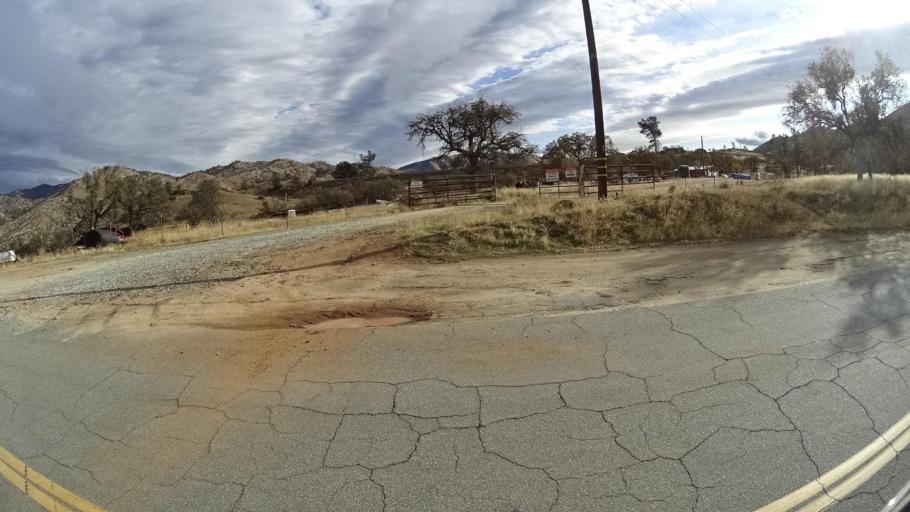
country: US
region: California
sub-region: Kern County
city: Golden Hills
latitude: 35.2000
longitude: -118.5409
